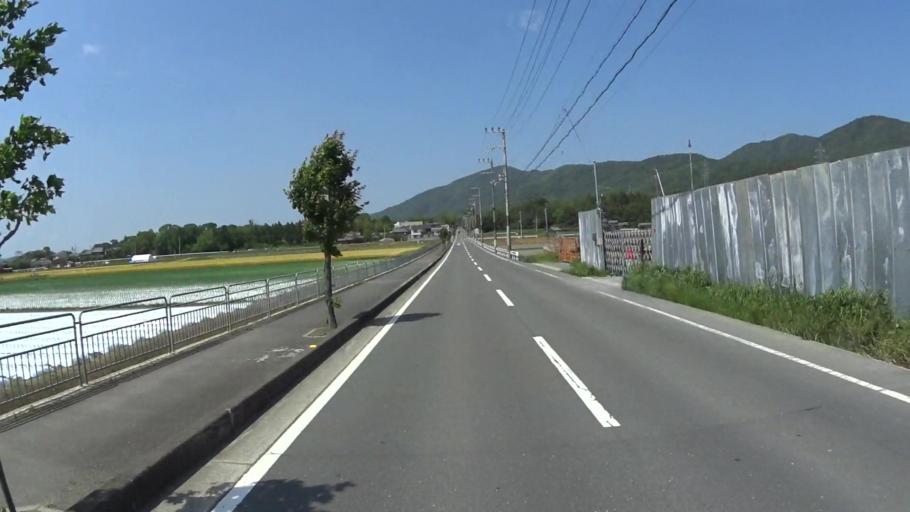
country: JP
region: Kyoto
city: Kameoka
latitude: 35.0374
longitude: 135.5749
